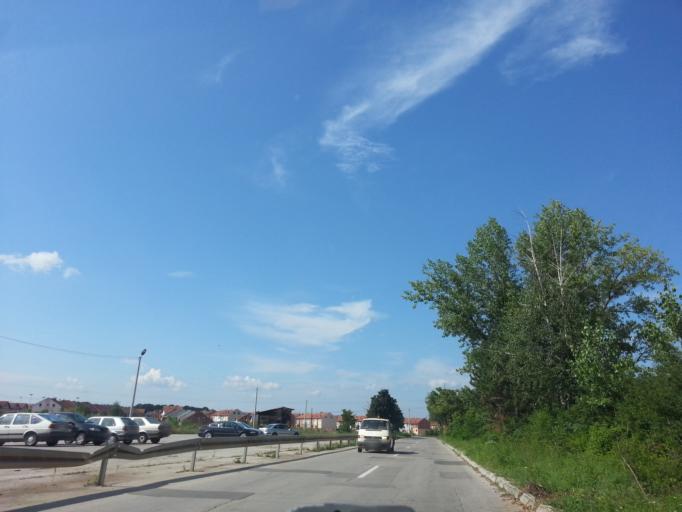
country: BA
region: Brcko
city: Brcko
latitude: 44.8550
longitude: 18.8208
